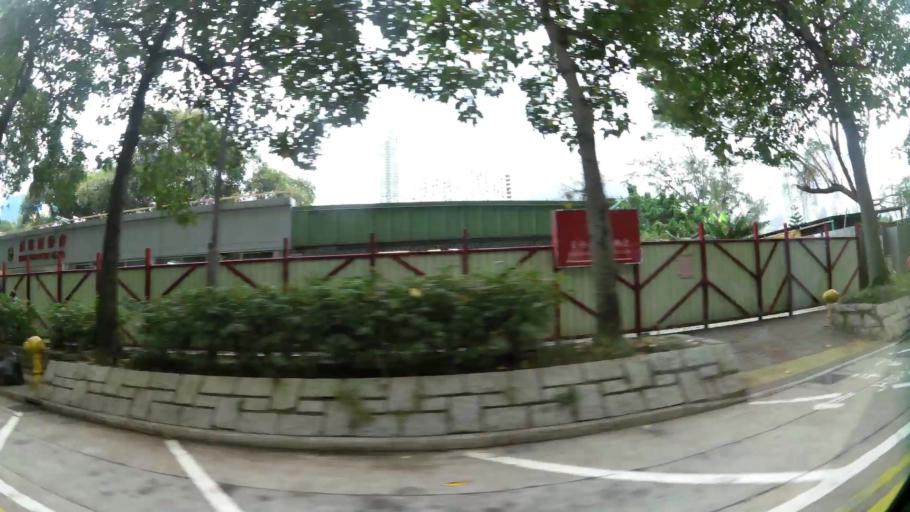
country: HK
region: Kowloon City
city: Kowloon
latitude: 22.3306
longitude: 114.2074
